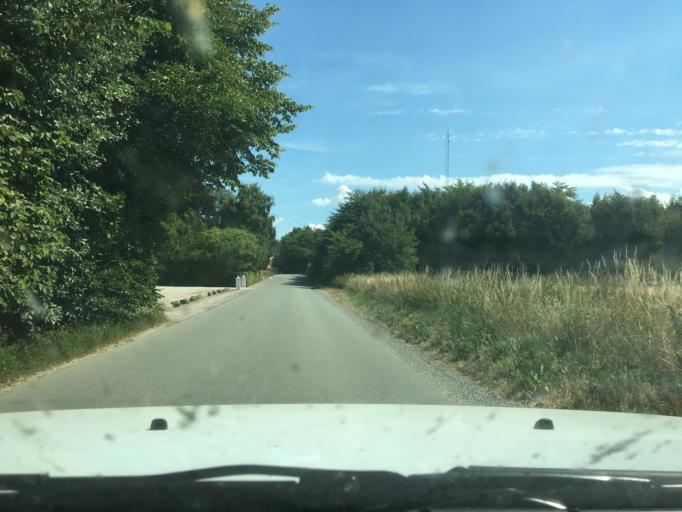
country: DK
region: Central Jutland
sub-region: Randers Kommune
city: Assentoft
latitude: 56.3625
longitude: 10.1369
